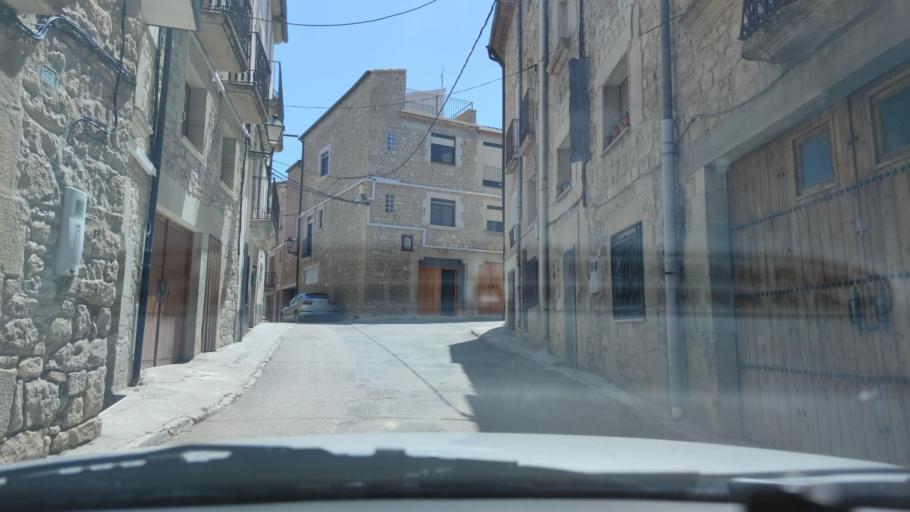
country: ES
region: Catalonia
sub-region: Provincia de Lleida
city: Fulleda
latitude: 41.4947
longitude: 1.0056
